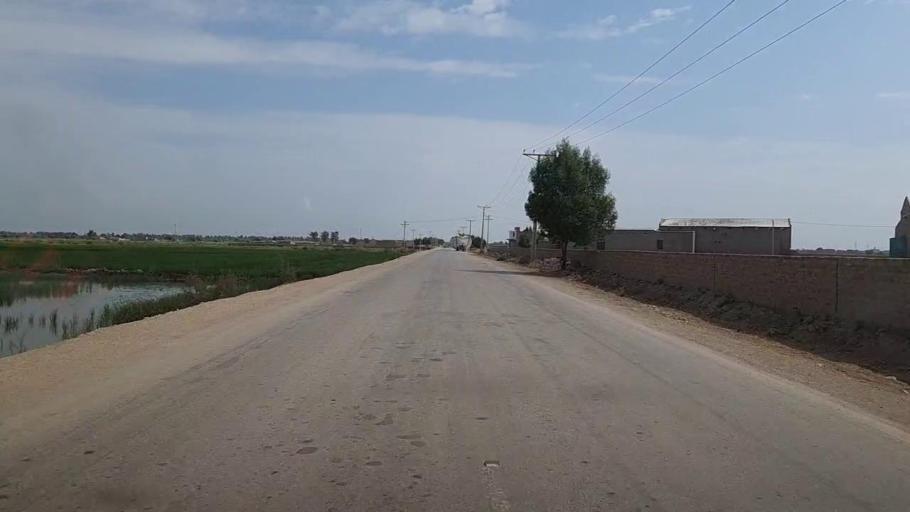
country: PK
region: Sindh
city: Thul
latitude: 28.2537
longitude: 68.7804
